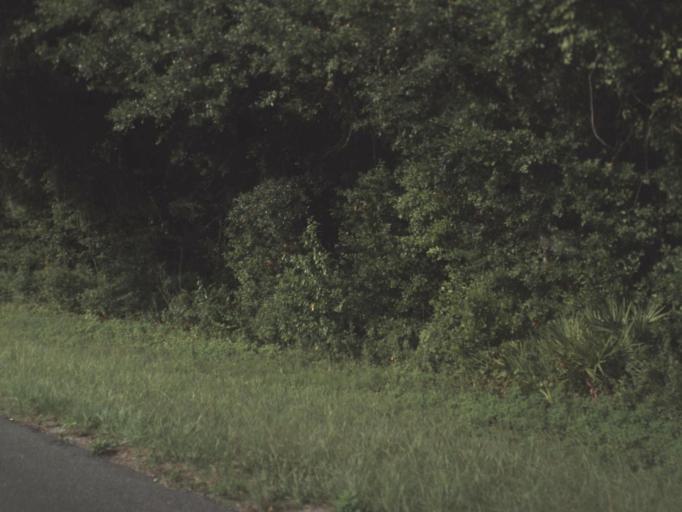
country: US
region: Florida
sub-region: Taylor County
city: Perry
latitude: 30.2516
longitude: -83.6228
